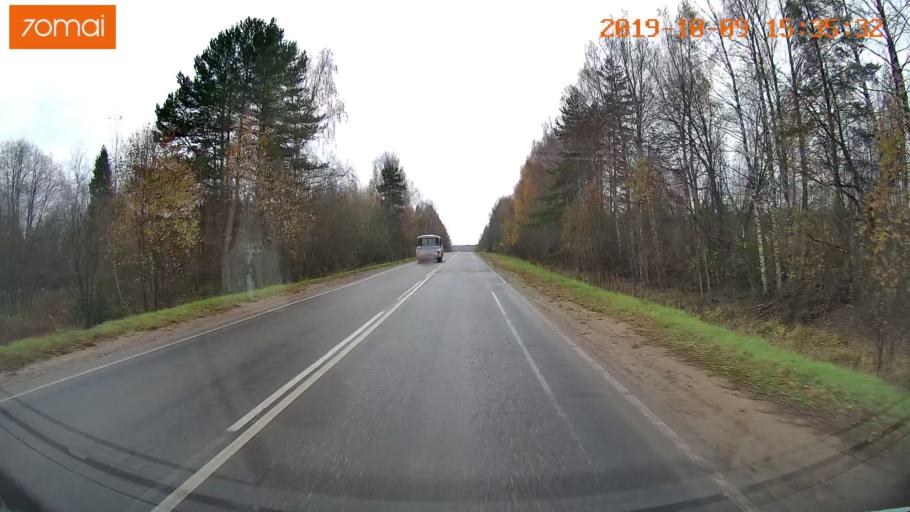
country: RU
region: Kostroma
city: Oktyabr'skiy
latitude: 57.9310
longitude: 41.2251
